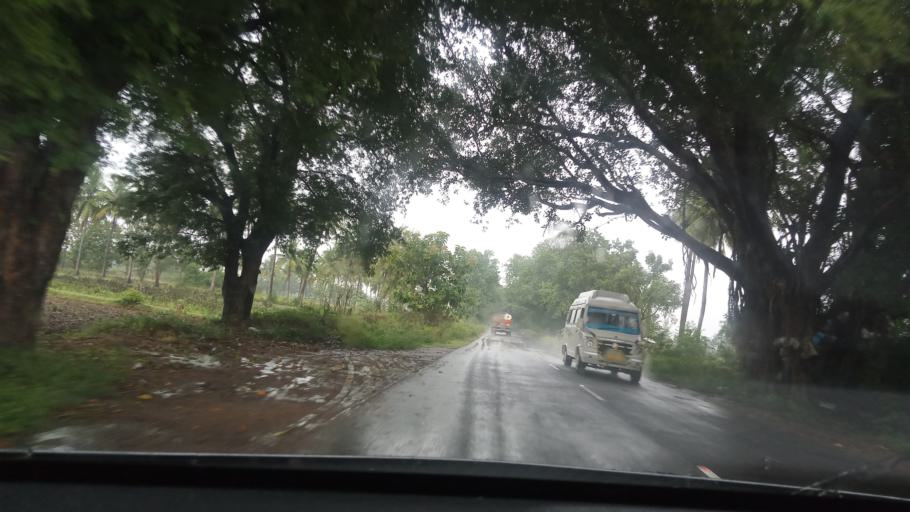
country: IN
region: Tamil Nadu
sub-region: Vellore
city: Kalavai
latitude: 12.8131
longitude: 79.4123
